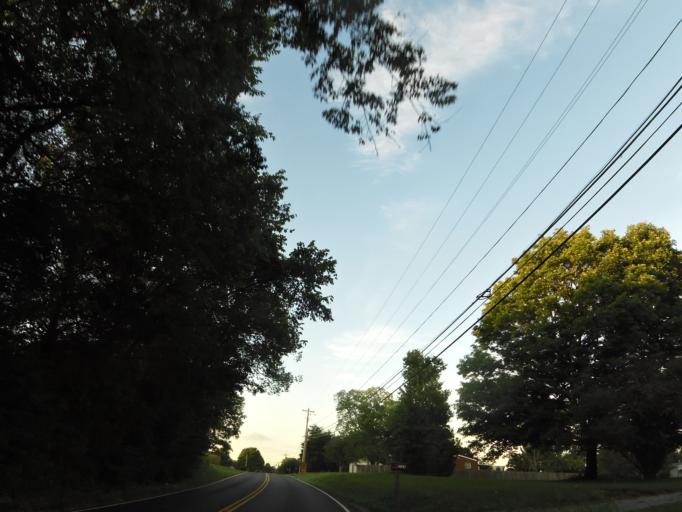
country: US
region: Tennessee
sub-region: Knox County
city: Farragut
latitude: 35.9397
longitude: -84.1390
